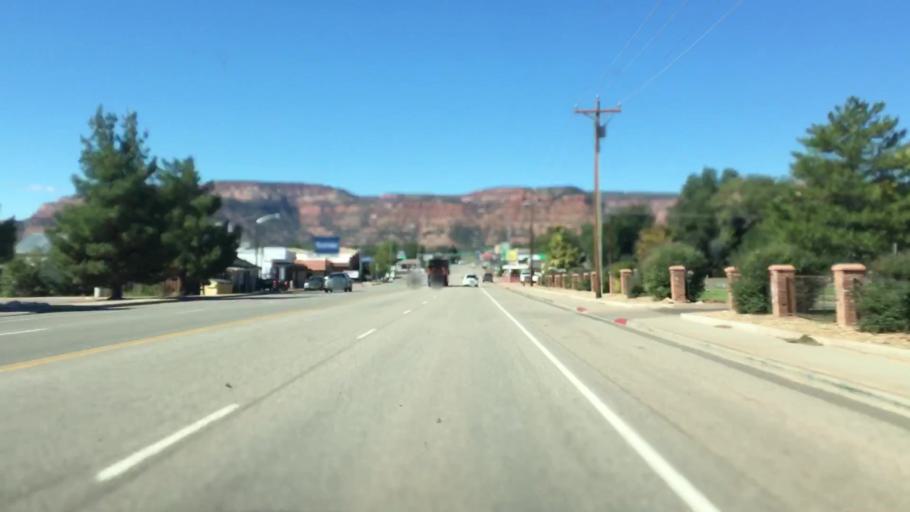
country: US
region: Utah
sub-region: Kane County
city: Kanab
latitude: 37.0431
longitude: -112.5185
